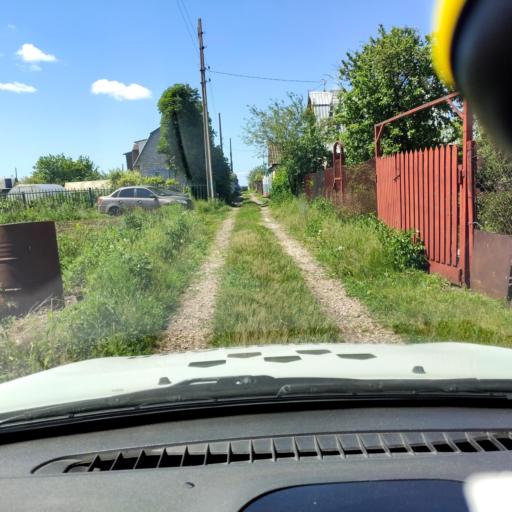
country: RU
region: Samara
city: Tol'yatti
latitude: 53.6110
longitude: 49.4491
